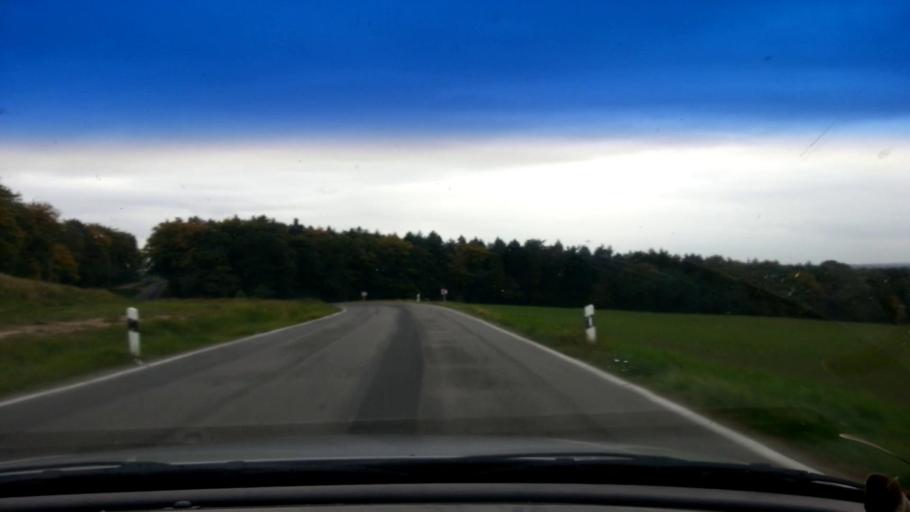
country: DE
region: Bavaria
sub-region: Upper Franconia
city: Priesendorf
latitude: 49.8996
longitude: 10.6561
